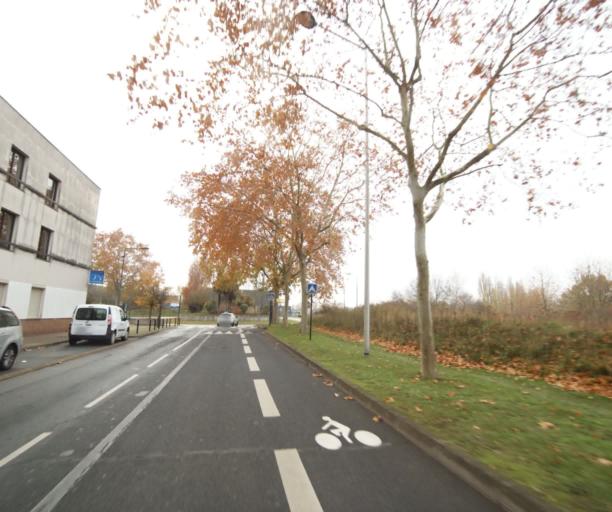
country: FR
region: Ile-de-France
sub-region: Departement de l'Essonne
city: Lisses
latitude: 48.6147
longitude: 2.4335
